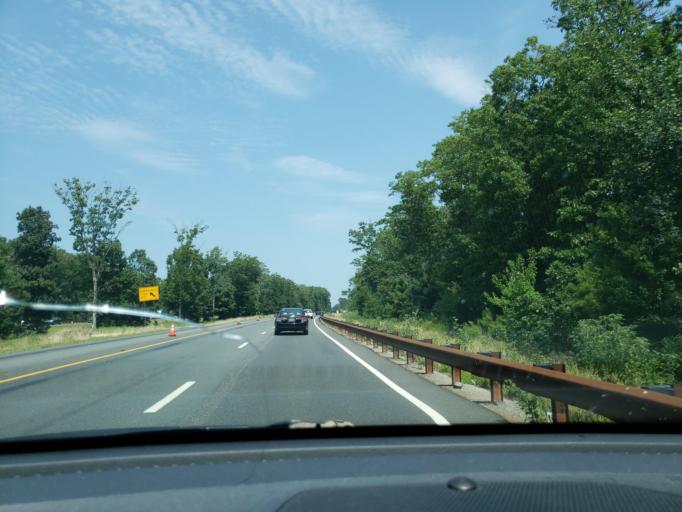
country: US
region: New Jersey
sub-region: Atlantic County
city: Linwood
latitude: 39.3526
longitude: -74.5962
